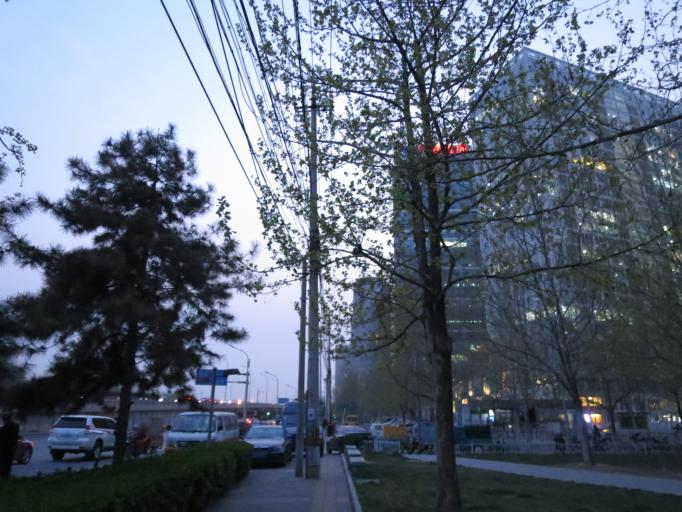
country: CN
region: Beijing
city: Chaowai
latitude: 39.9029
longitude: 116.4481
